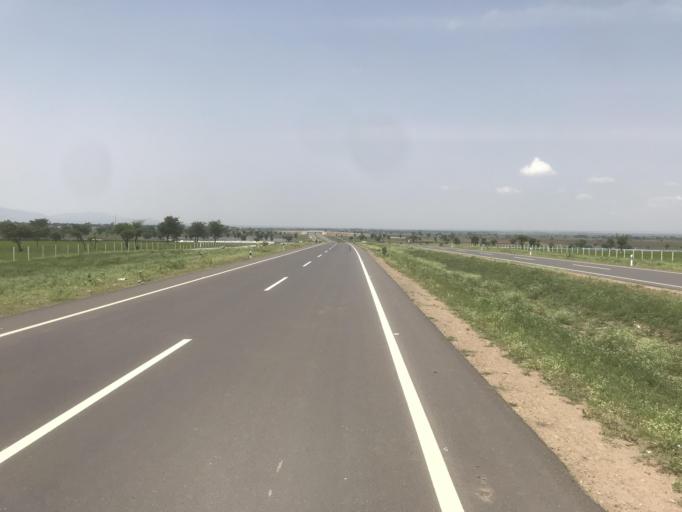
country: ET
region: Oromiya
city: Mojo
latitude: 8.4612
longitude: 39.0357
